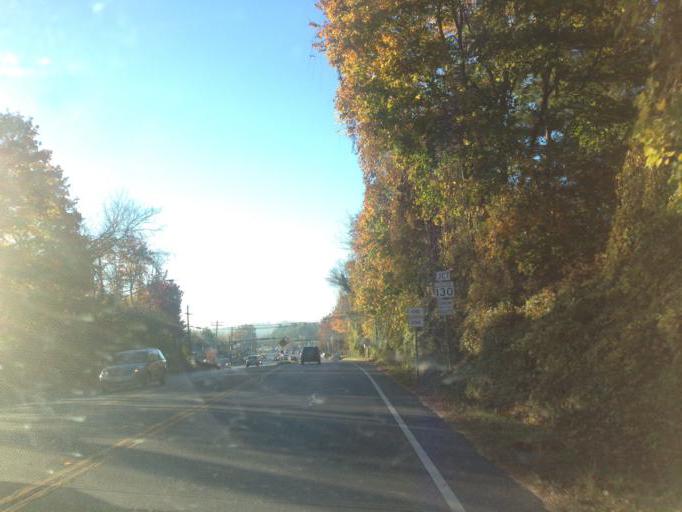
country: US
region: Maryland
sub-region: Baltimore County
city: Mays Chapel
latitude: 39.4226
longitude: -76.6712
